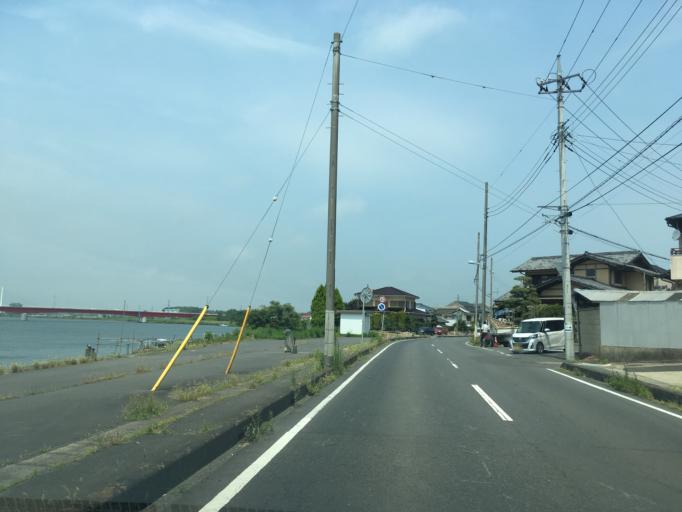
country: JP
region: Ibaraki
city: Oarai
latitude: 36.3411
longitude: 140.5822
